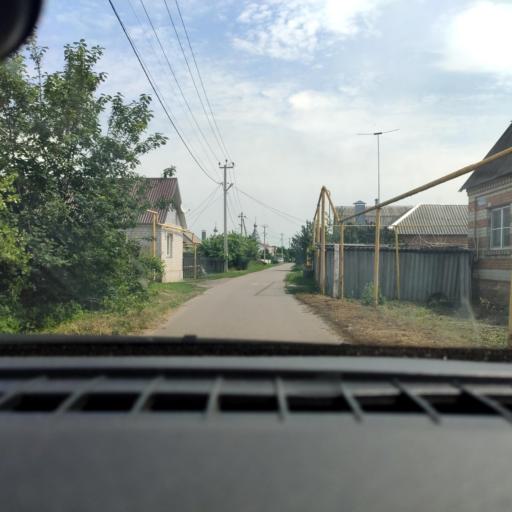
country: RU
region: Voronezj
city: Novaya Usman'
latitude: 51.6791
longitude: 39.3647
